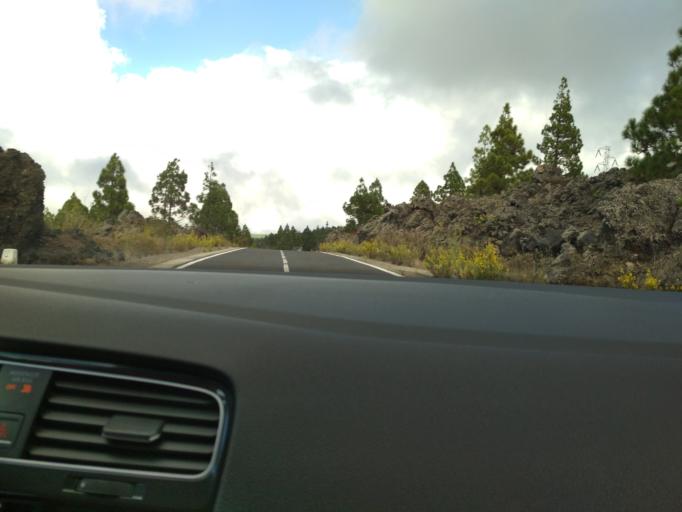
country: ES
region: Canary Islands
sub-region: Provincia de Santa Cruz de Tenerife
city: Garachico
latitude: 28.3304
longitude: -16.7721
